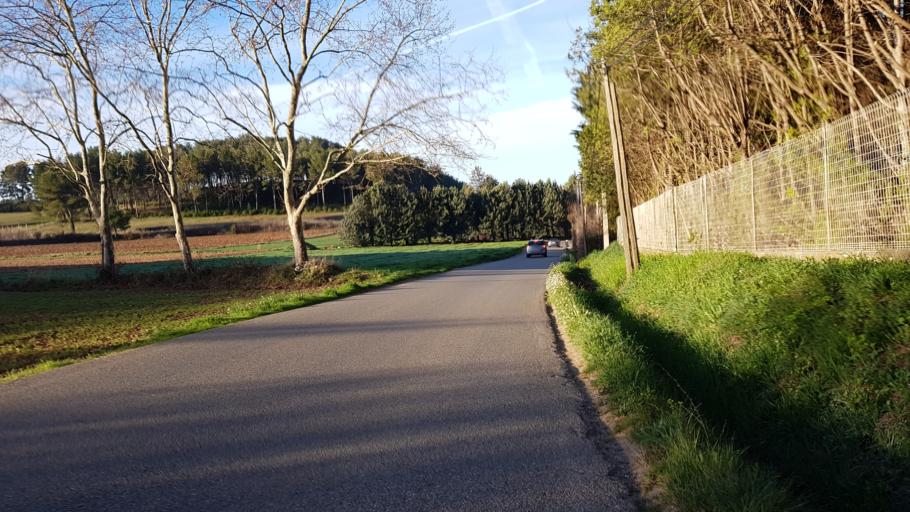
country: FR
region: Provence-Alpes-Cote d'Azur
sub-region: Departement des Bouches-du-Rhone
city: Bouc-Bel-Air
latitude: 43.4924
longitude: 5.3927
